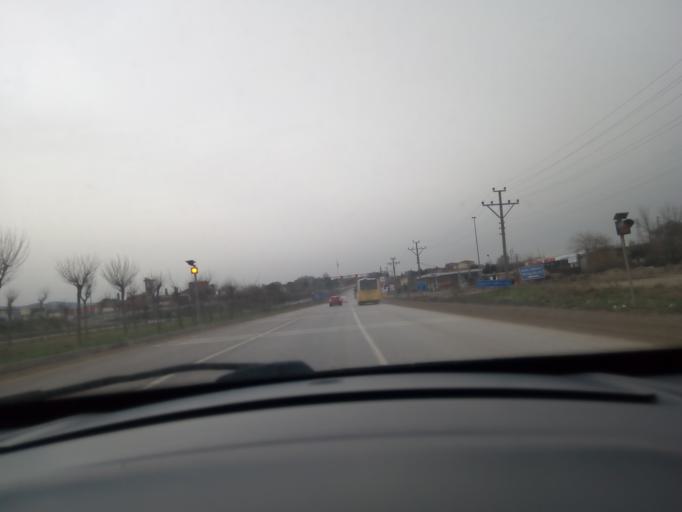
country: TR
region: Balikesir
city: Susurluk
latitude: 39.9535
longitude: 28.1707
